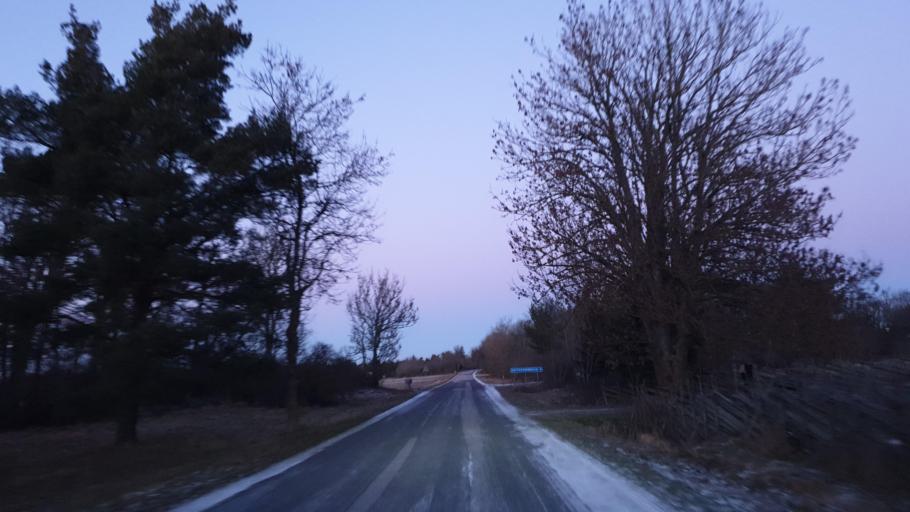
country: SE
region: Gotland
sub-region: Gotland
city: Slite
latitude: 57.4059
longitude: 18.8045
